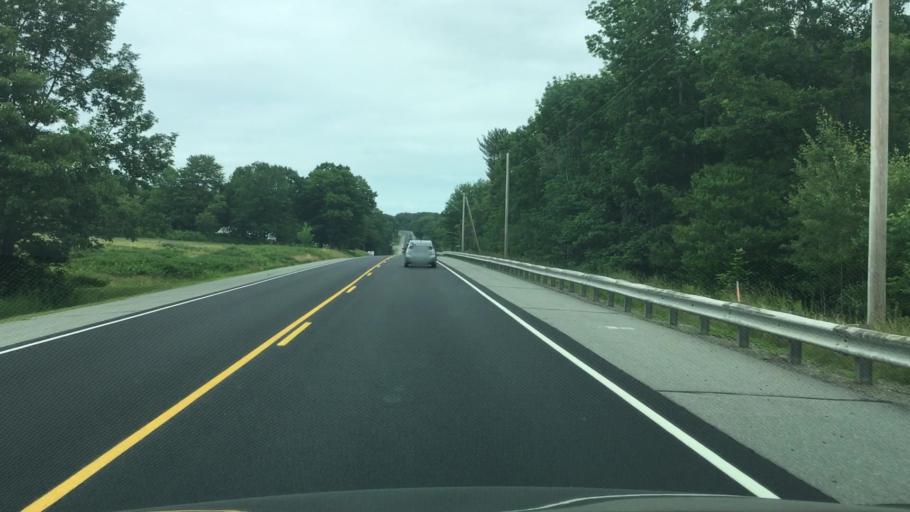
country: US
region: Maine
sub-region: Waldo County
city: Stockton Springs
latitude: 44.5021
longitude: -68.8258
